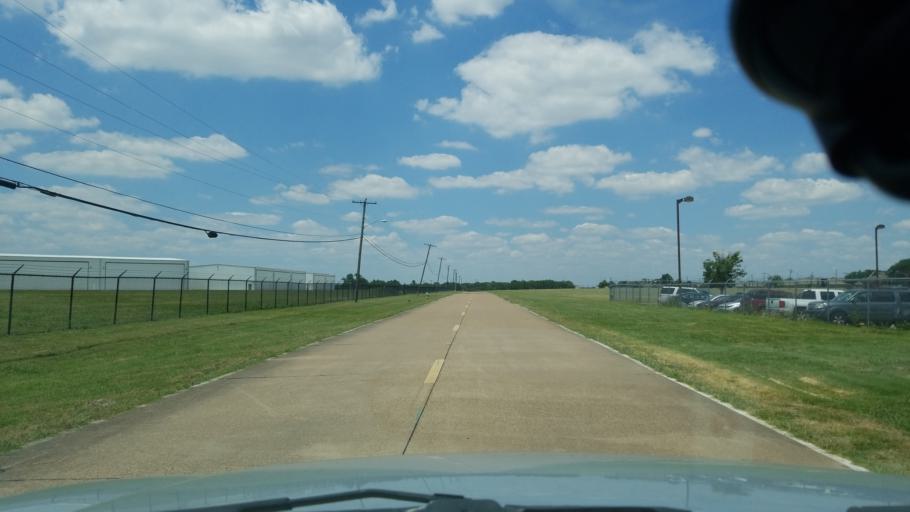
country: US
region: Texas
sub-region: Dallas County
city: Duncanville
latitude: 32.6792
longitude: -96.8590
